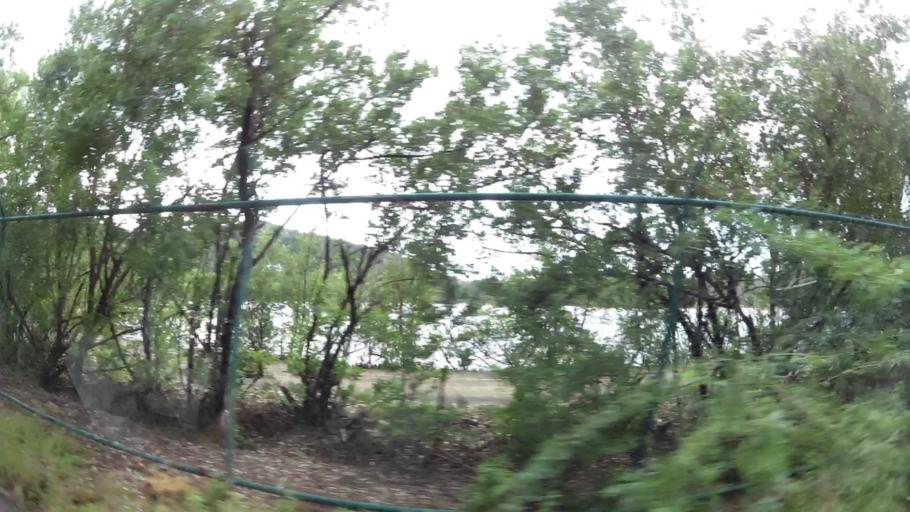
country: AG
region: Saint John
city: Saint John's
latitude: 17.1206
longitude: -61.8905
